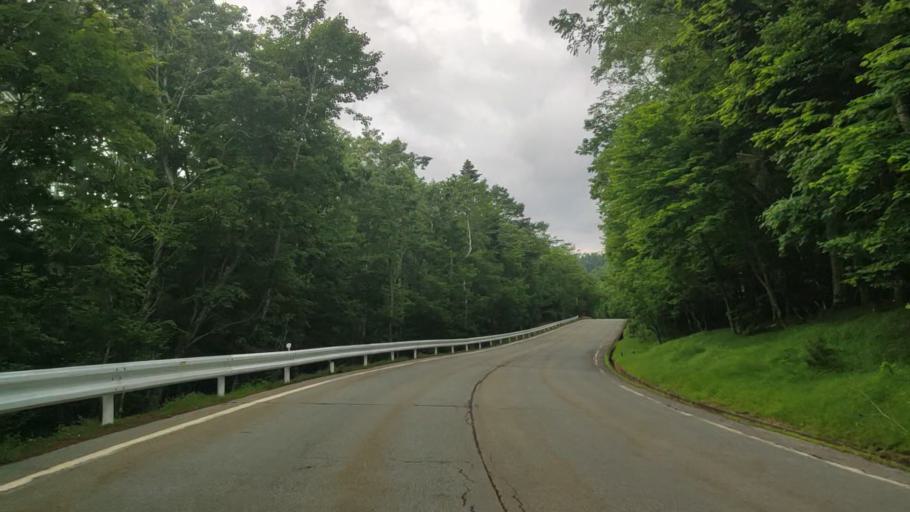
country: JP
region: Yamanashi
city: Fujikawaguchiko
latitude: 35.4160
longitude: 138.7203
